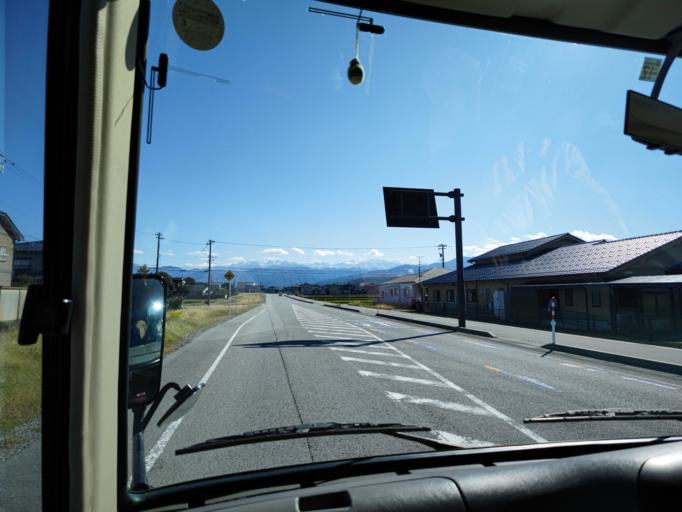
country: JP
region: Toyama
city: Nyuzen
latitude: 36.8812
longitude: 137.4413
